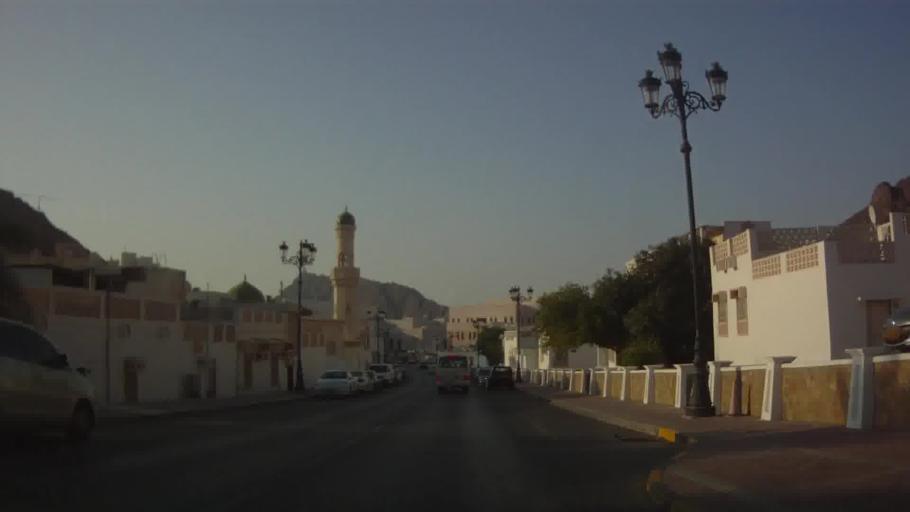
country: OM
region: Muhafazat Masqat
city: Muscat
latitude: 23.6095
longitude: 58.5956
